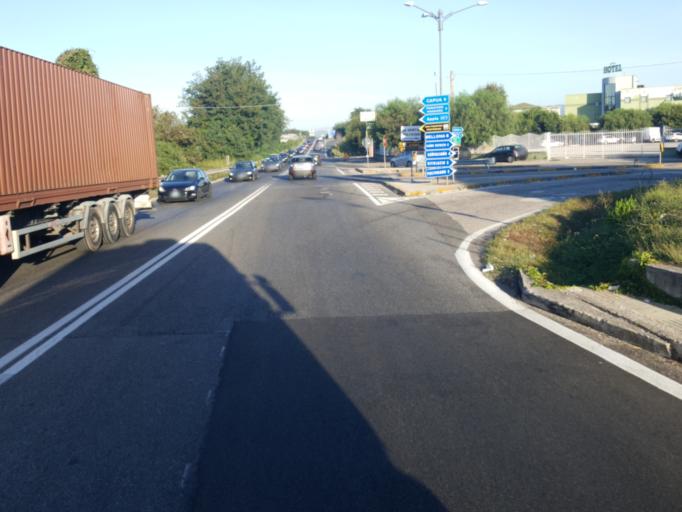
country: IT
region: Campania
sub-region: Provincia di Caserta
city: Pignataro Maggiore
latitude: 41.1612
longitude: 14.1760
